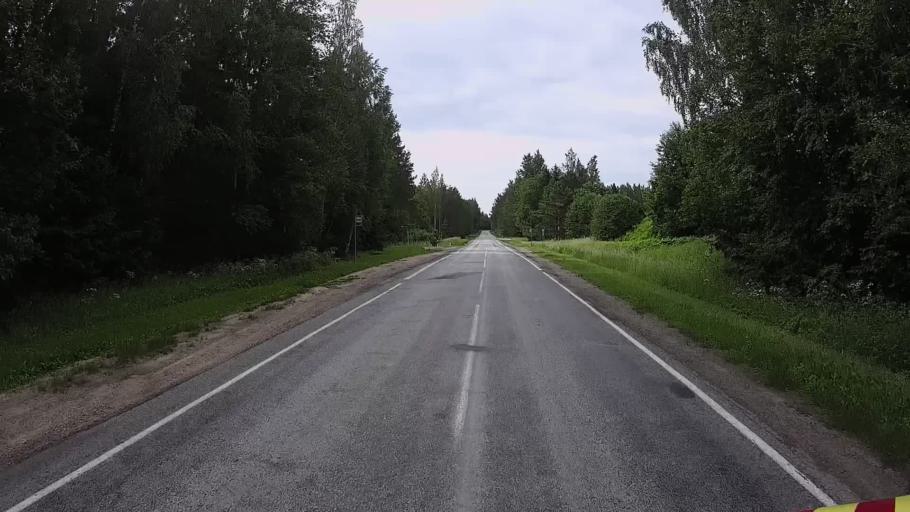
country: EE
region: Viljandimaa
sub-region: Karksi vald
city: Karksi-Nuia
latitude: 58.2164
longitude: 25.6194
